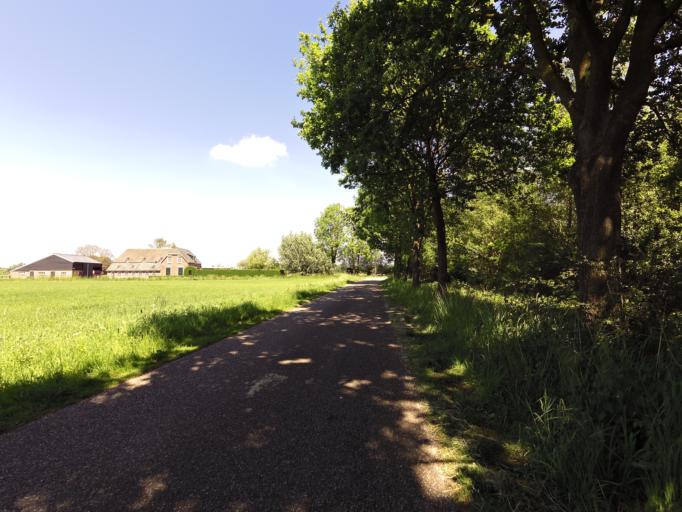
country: NL
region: Gelderland
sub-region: Gemeente Bronckhorst
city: Hengelo
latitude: 52.0625
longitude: 6.2788
